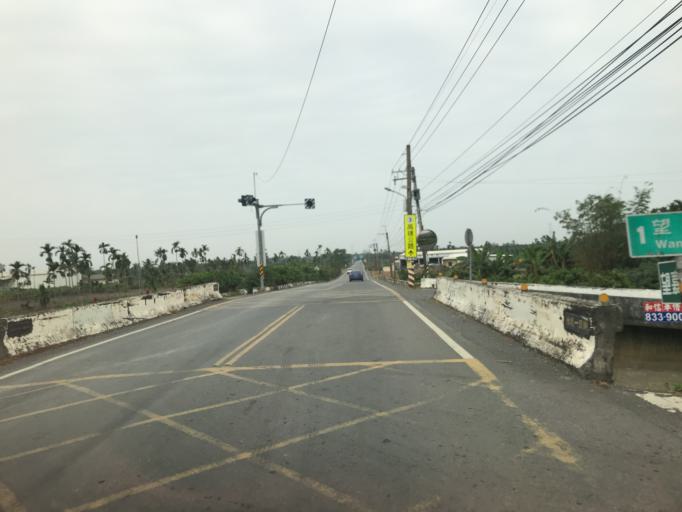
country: TW
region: Taiwan
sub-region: Pingtung
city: Pingtung
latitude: 22.4681
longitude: 120.6094
